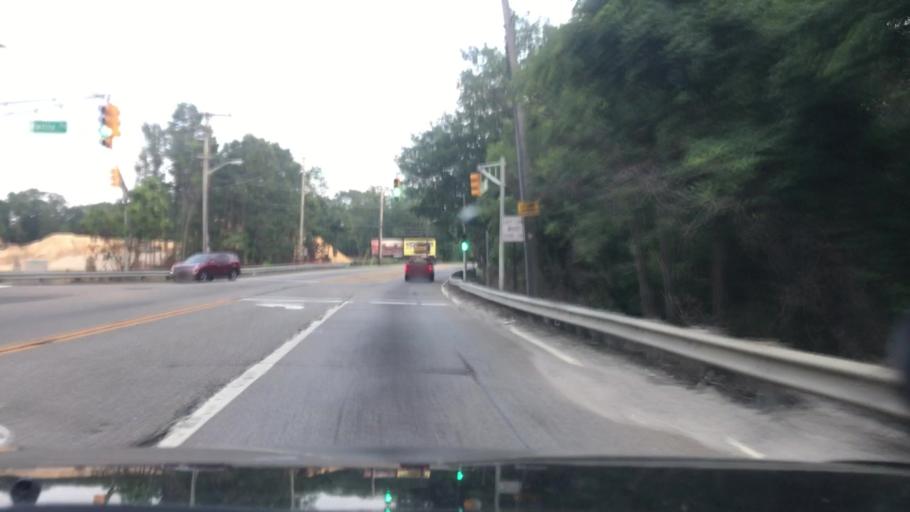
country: US
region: New Jersey
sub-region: Ocean County
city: Silver Ridge
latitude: 40.0005
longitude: -74.2126
